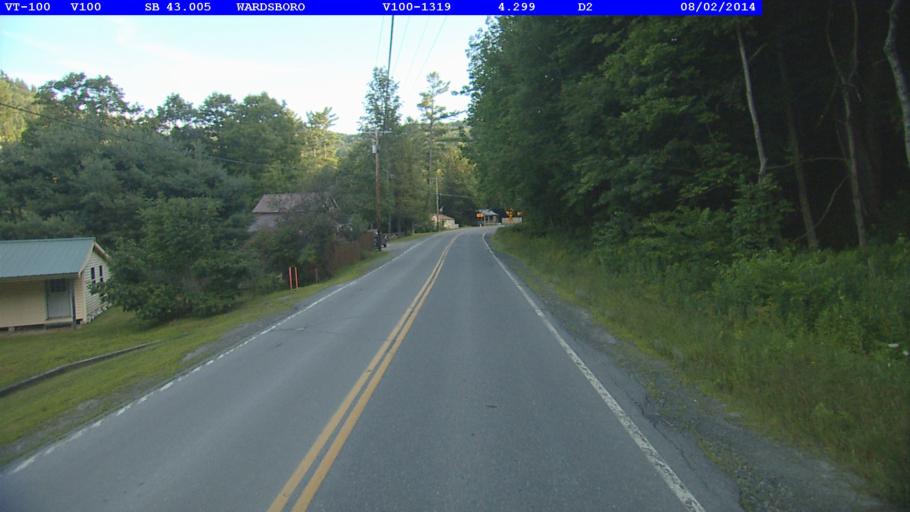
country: US
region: Vermont
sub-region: Windham County
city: Dover
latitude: 43.0265
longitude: -72.8201
